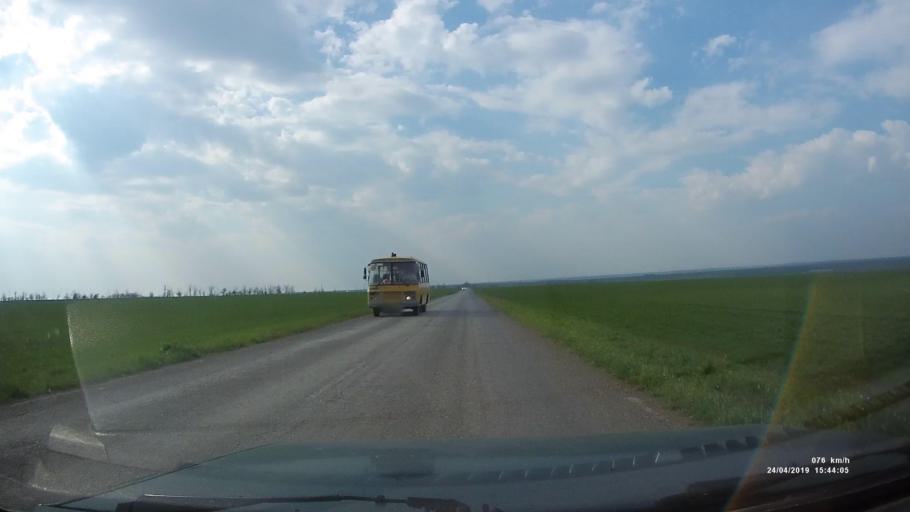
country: RU
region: Kalmykiya
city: Yashalta
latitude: 46.5867
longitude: 42.7625
